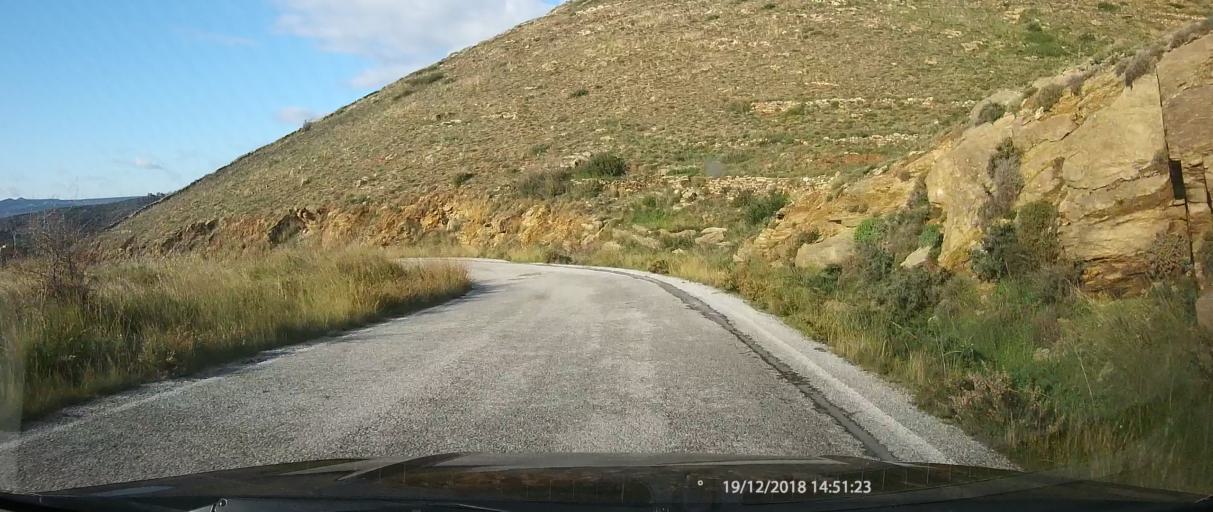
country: GR
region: Peloponnese
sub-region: Nomos Lakonias
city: Gytheio
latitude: 36.4580
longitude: 22.4486
